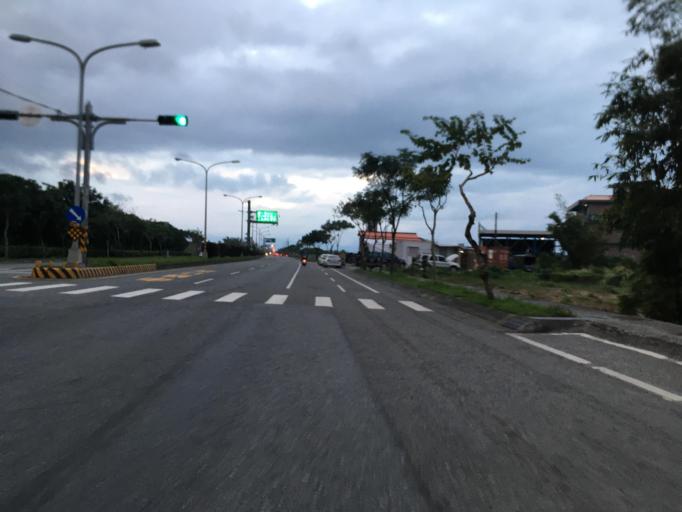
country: TW
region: Taiwan
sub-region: Yilan
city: Yilan
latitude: 24.6152
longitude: 121.8490
